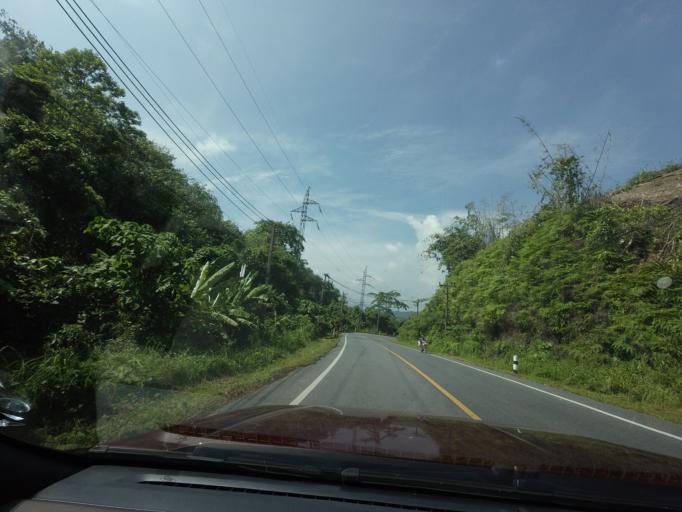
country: TH
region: Yala
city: Betong
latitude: 5.8365
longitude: 101.1193
